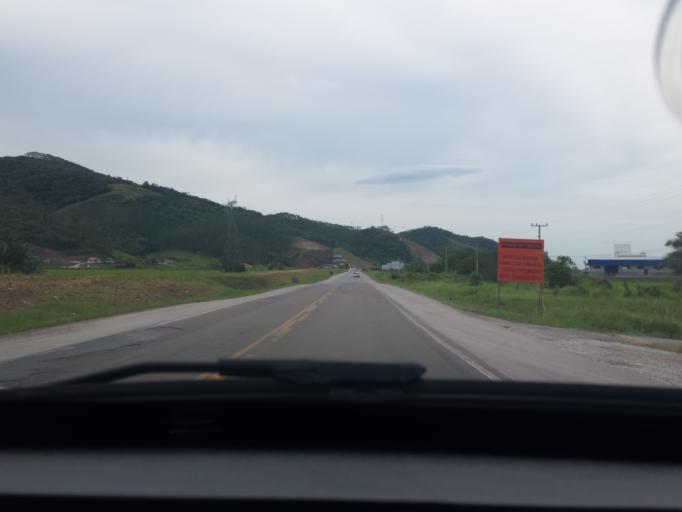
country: BR
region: Santa Catarina
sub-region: Gaspar
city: Gaspar
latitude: -26.8981
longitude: -48.9247
